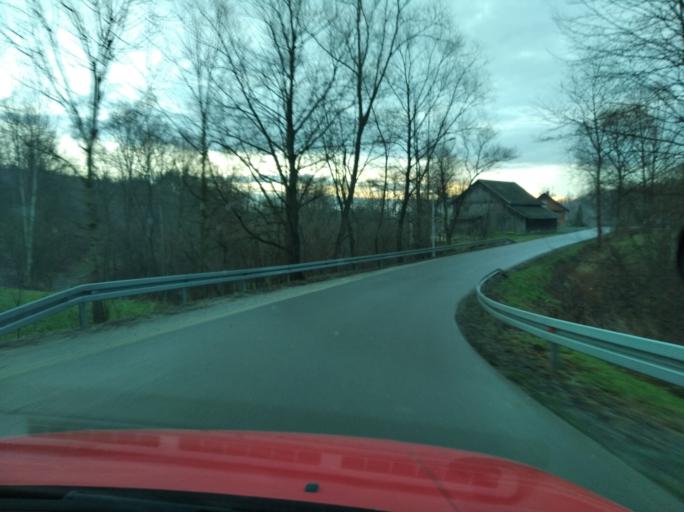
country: PL
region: Subcarpathian Voivodeship
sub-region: Powiat strzyzowski
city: Jawornik
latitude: 49.8744
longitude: 21.8659
